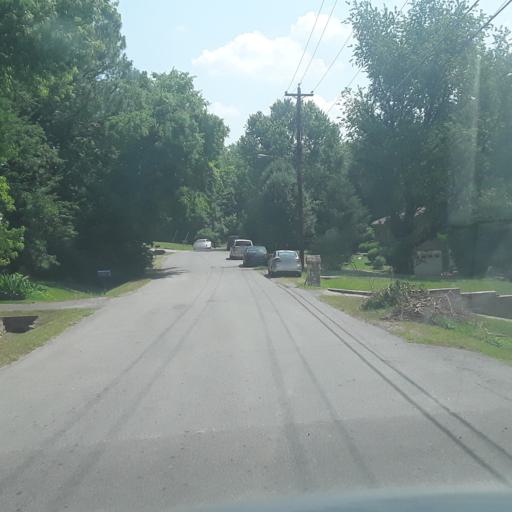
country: US
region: Tennessee
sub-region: Williamson County
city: Brentwood Estates
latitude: 36.0559
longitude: -86.7098
